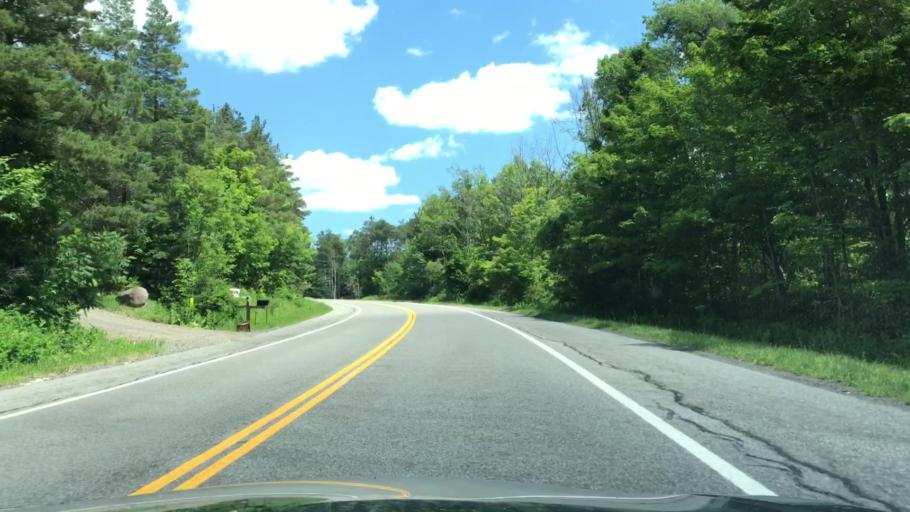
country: US
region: New York
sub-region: Erie County
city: East Aurora
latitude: 42.7647
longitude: -78.5127
